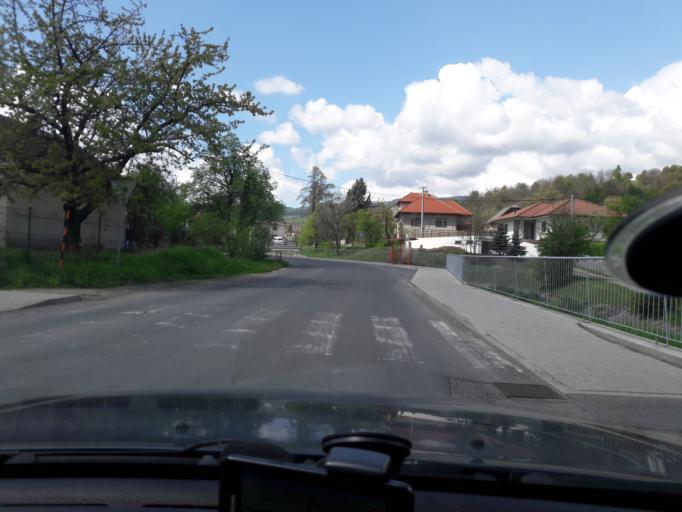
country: SK
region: Banskobystricky
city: Hrinova
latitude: 48.5697
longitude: 19.5055
